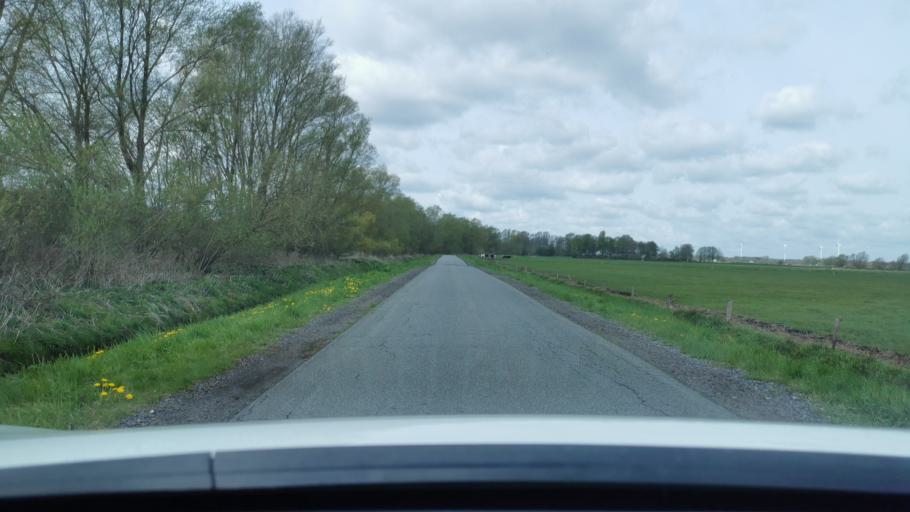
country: DE
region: Schleswig-Holstein
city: Oldenbuttel
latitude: 54.1816
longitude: 9.4509
